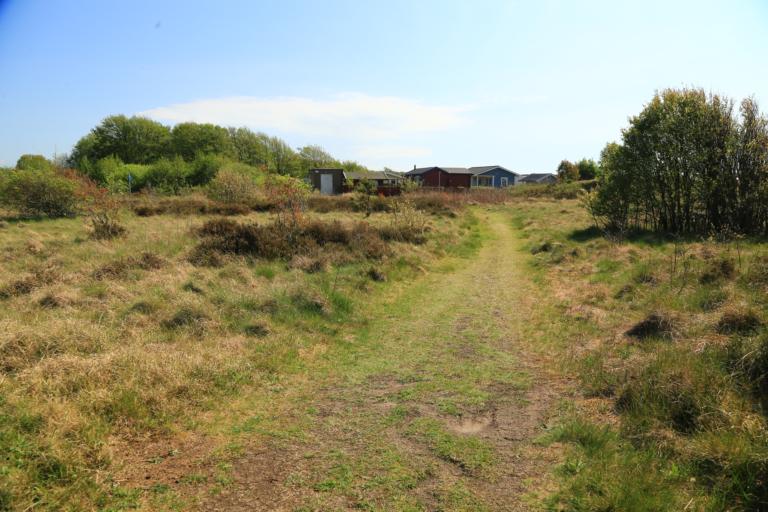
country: SE
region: Halland
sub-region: Varbergs Kommun
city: Traslovslage
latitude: 57.0808
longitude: 12.2673
